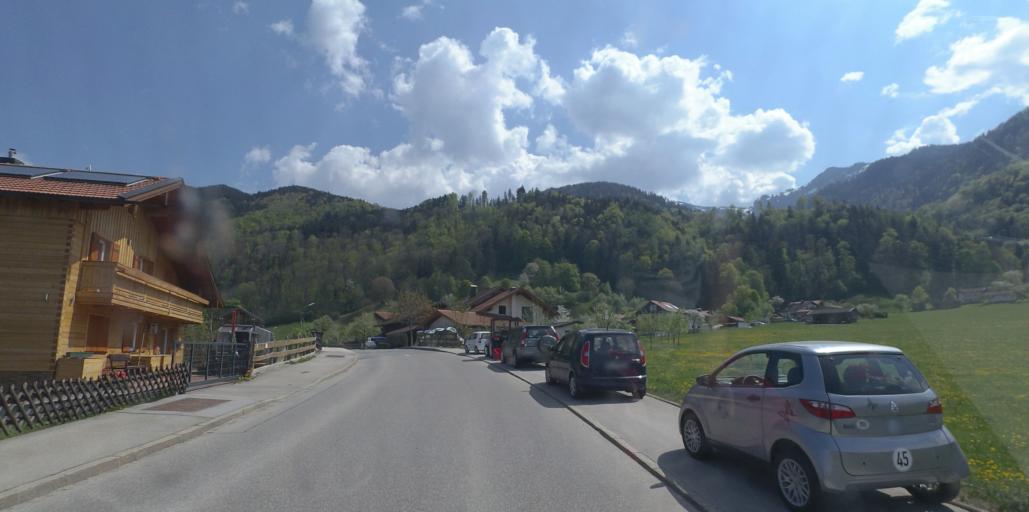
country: DE
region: Bavaria
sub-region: Upper Bavaria
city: Staudach-Egerndach
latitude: 47.7788
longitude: 12.4883
